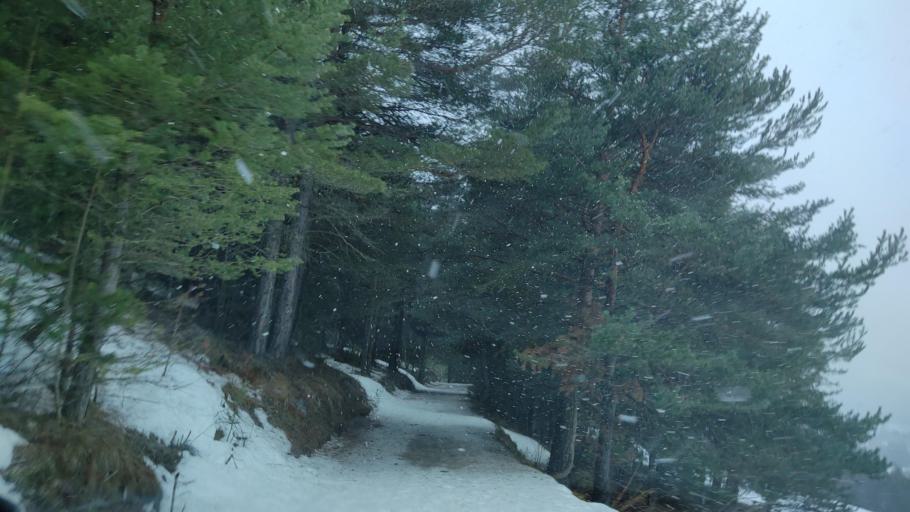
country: FR
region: Rhone-Alpes
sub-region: Departement de la Savoie
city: Modane
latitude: 45.2286
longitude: 6.7863
